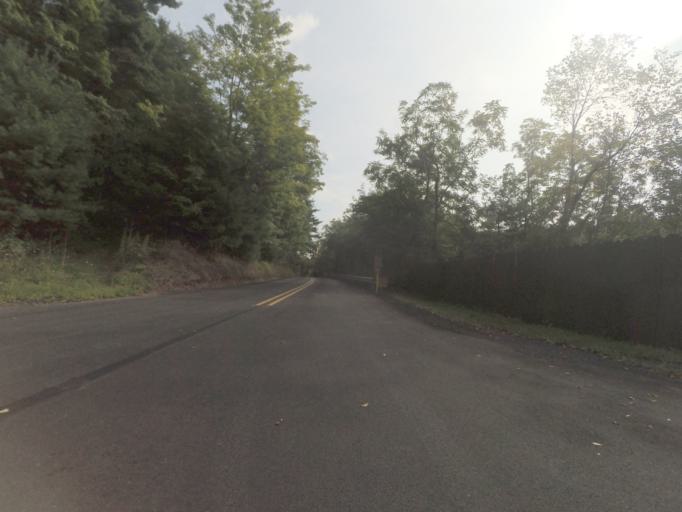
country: US
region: Pennsylvania
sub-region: Centre County
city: Milesburg
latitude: 41.0033
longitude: -77.7950
